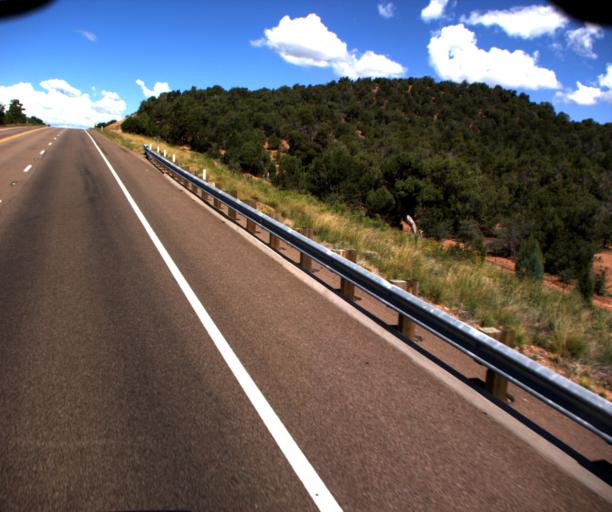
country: US
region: Arizona
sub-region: Navajo County
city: Linden
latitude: 34.2937
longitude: -110.1841
